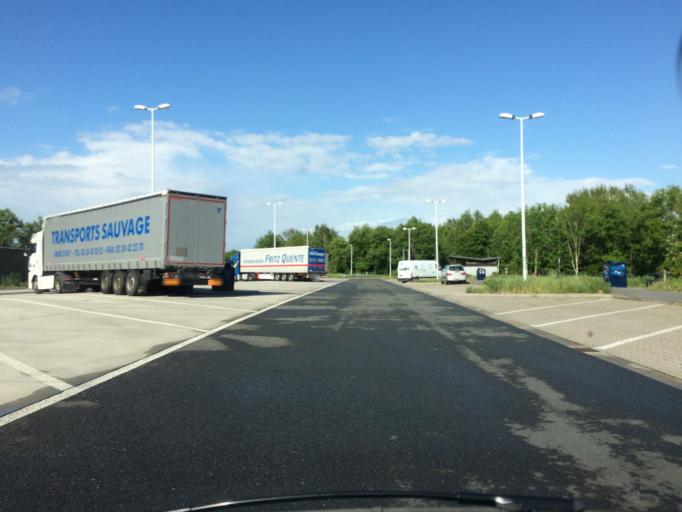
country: DE
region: North Rhine-Westphalia
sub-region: Regierungsbezirk Munster
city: Dulmen
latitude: 51.8690
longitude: 7.3230
